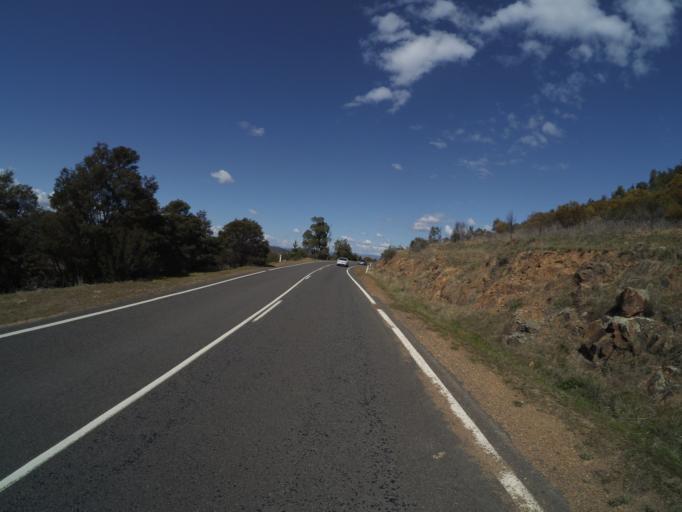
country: AU
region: Australian Capital Territory
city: Macquarie
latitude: -35.3059
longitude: 148.9480
